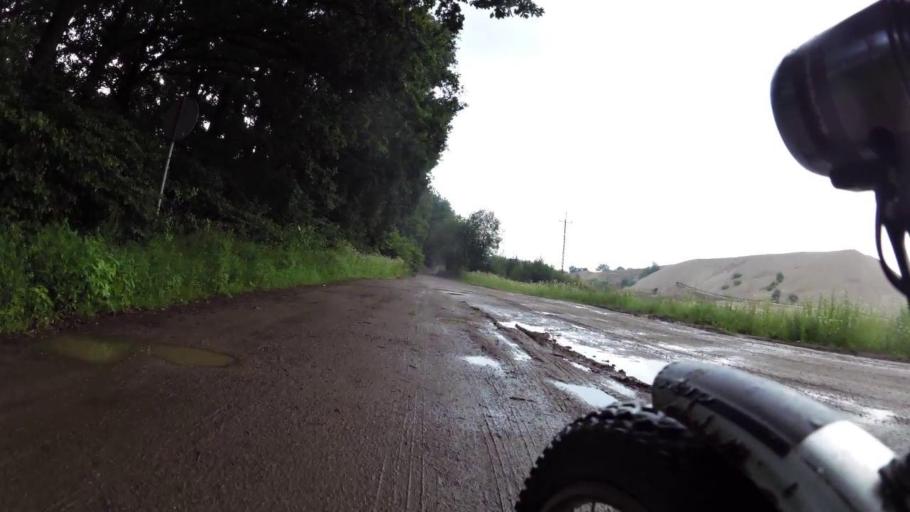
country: PL
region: West Pomeranian Voivodeship
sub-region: Powiat lobeski
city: Lobez
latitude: 53.7247
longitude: 15.6827
